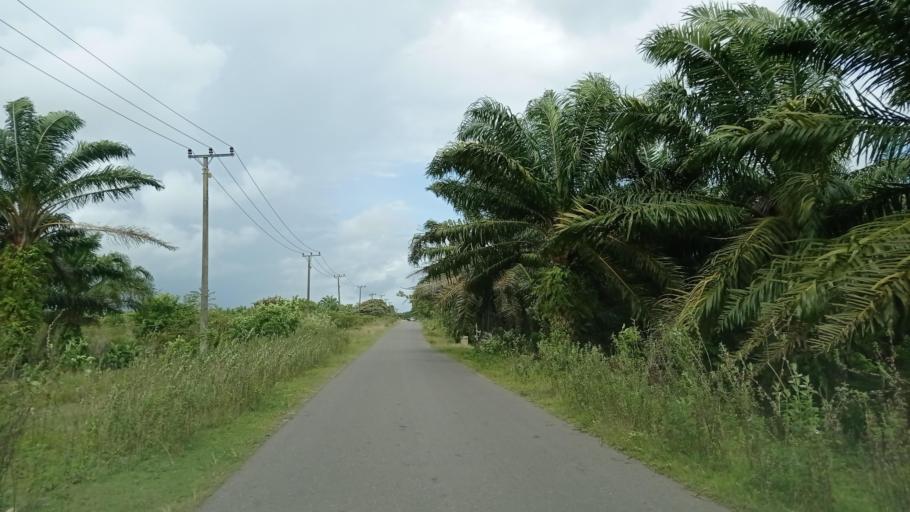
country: ID
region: Bengkulu
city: Ipuh
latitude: -2.5641
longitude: 101.1125
